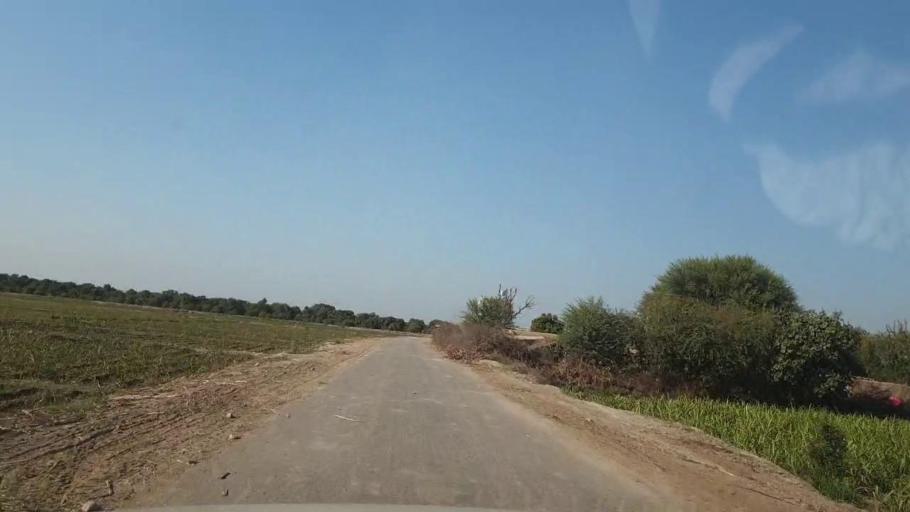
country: PK
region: Sindh
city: Tando Allahyar
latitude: 25.4867
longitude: 68.6564
